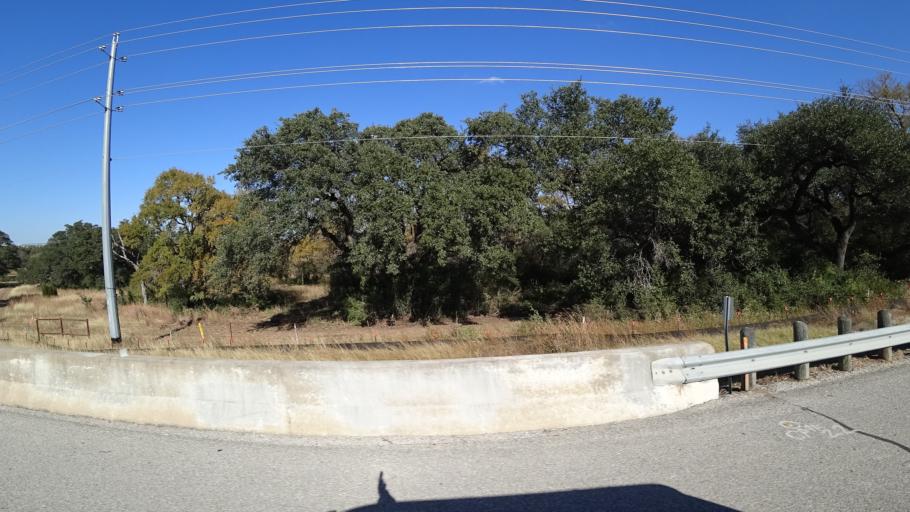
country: US
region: Texas
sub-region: Williamson County
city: Jollyville
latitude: 30.4517
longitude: -97.7492
